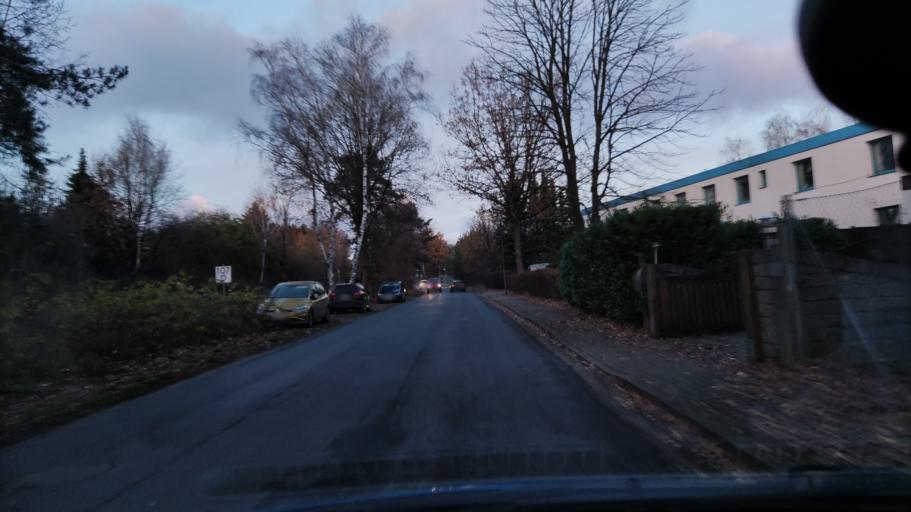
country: DE
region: Lower Saxony
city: Schneverdingen
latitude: 53.1228
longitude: 9.8069
